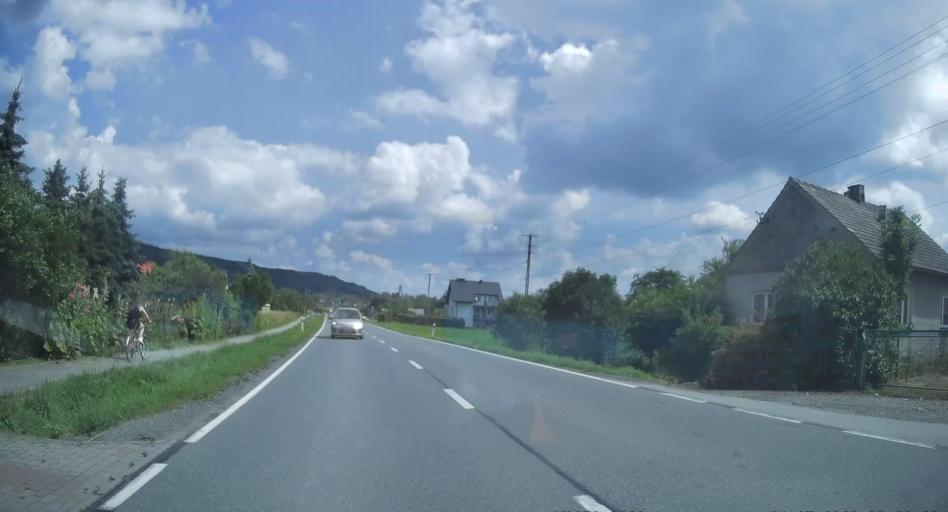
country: PL
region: Lesser Poland Voivodeship
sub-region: Powiat tarnowski
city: Wielka Wies
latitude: 49.9065
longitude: 20.8181
